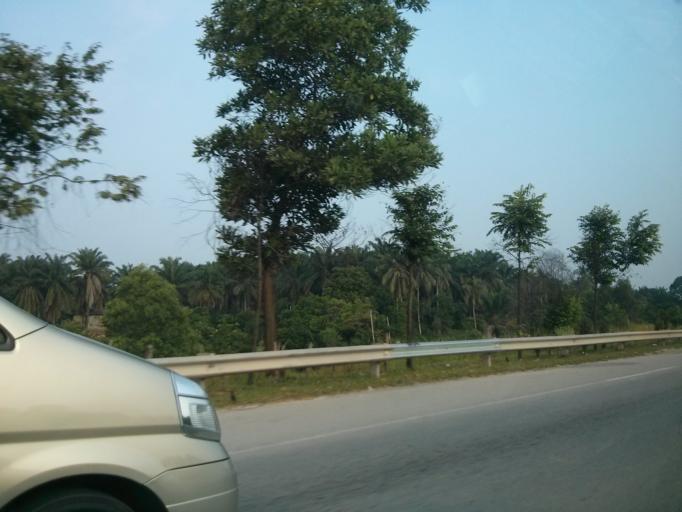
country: MY
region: Putrajaya
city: Putrajaya
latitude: 2.8878
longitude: 101.6596
